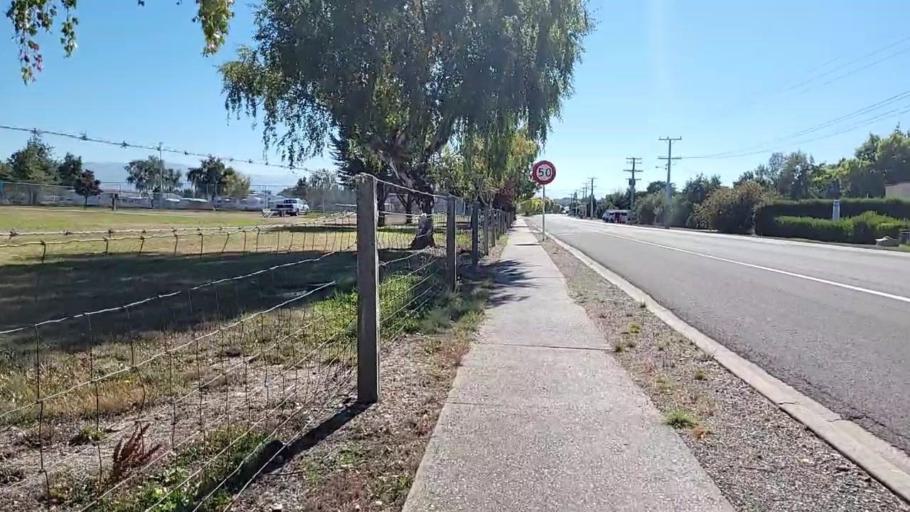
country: NZ
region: Otago
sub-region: Queenstown-Lakes District
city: Wanaka
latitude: -45.1009
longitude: 169.5965
